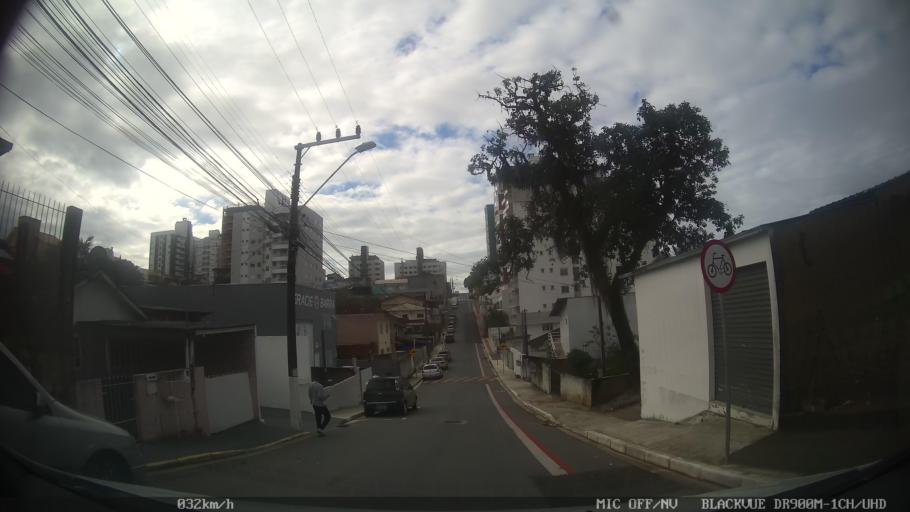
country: BR
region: Santa Catarina
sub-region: Sao Jose
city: Campinas
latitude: -27.5771
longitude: -48.6058
